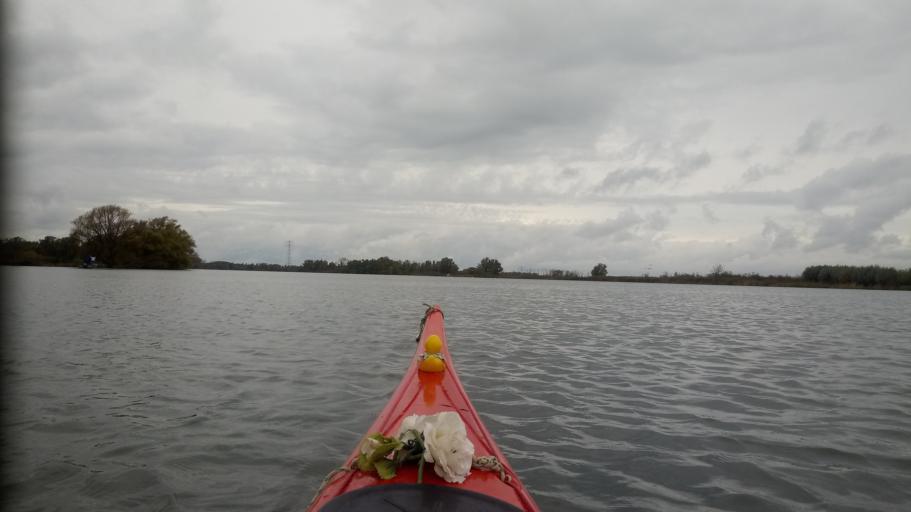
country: NL
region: North Brabant
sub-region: Gemeente Made en Drimmelen
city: Drimmelen
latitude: 51.7548
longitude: 4.8180
